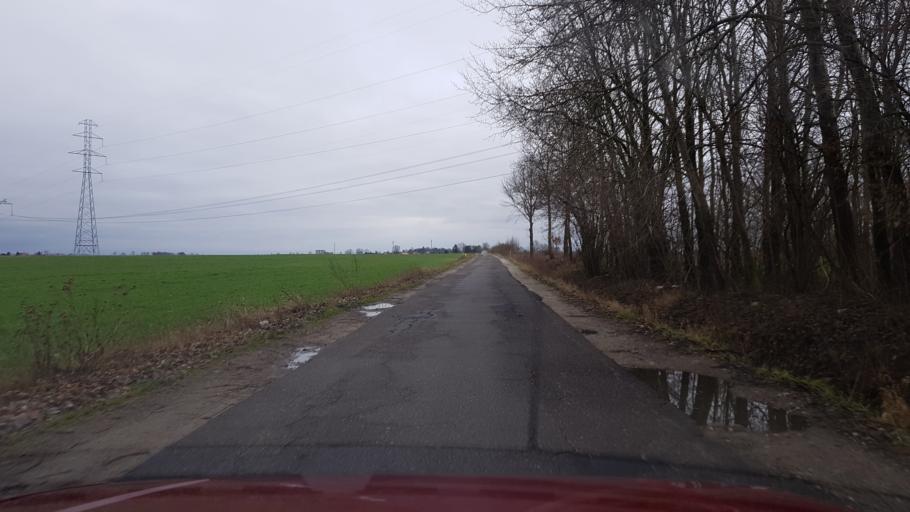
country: PL
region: West Pomeranian Voivodeship
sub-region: Powiat koszalinski
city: Mielno
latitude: 54.1475
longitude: 16.0302
